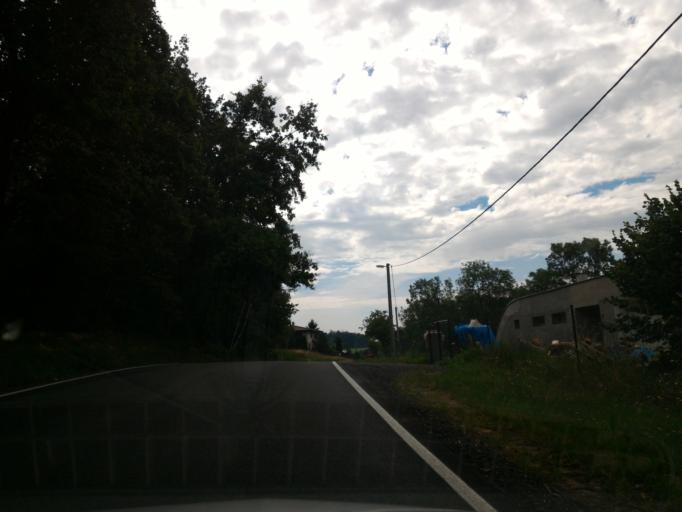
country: CZ
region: Vysocina
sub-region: Okres Jihlava
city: Telc
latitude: 49.1648
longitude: 15.5024
